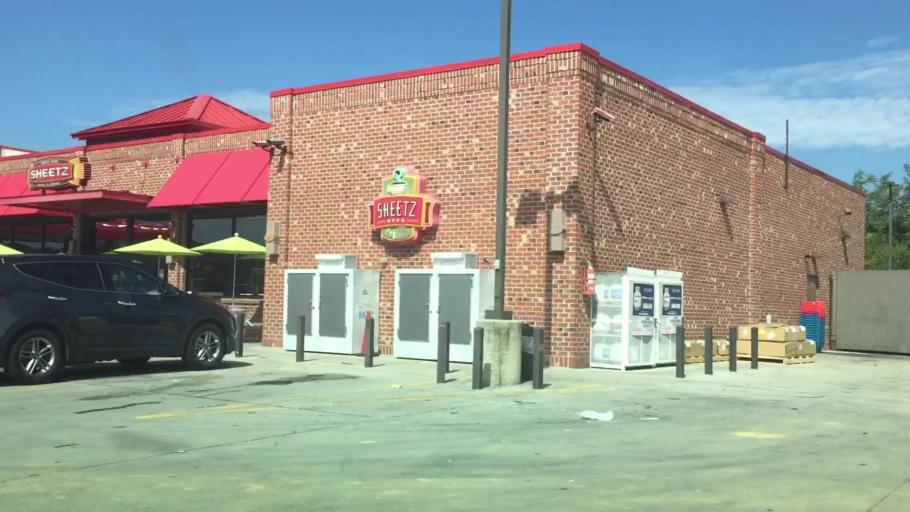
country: US
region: Virginia
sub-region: Wythe County
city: Wytheville
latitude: 36.9595
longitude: -81.0953
